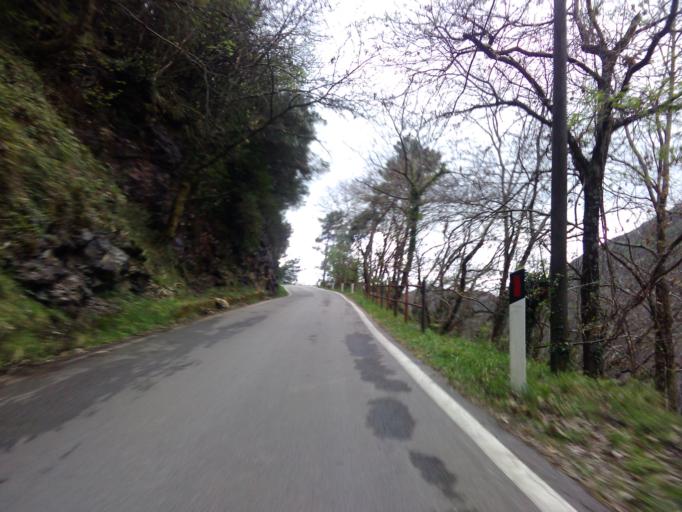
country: IT
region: Tuscany
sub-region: Provincia di Lucca
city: Pontestazzemese
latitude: 43.9709
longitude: 10.2828
